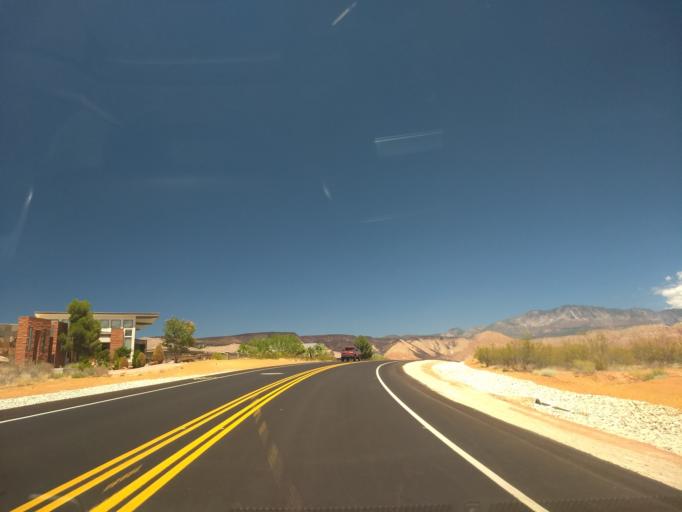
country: US
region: Utah
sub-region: Washington County
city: Washington
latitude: 37.1545
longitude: -113.5193
